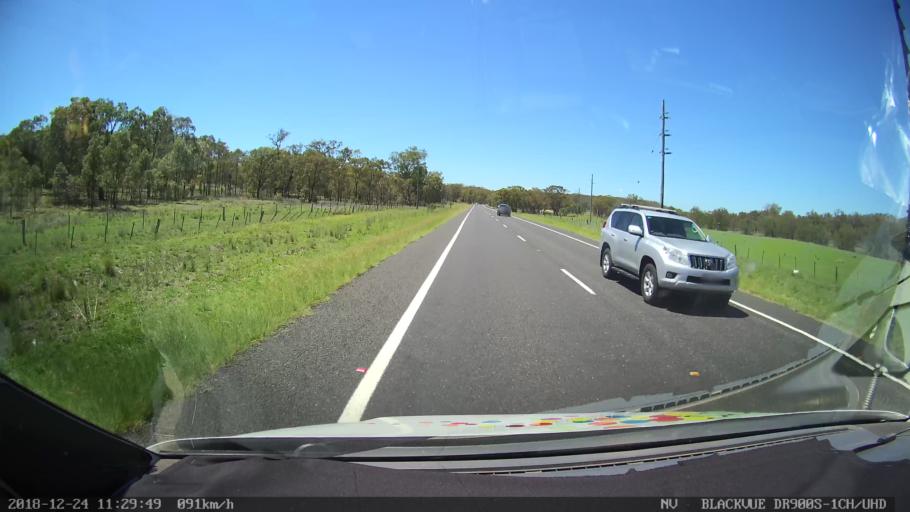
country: AU
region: New South Wales
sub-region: Upper Hunter Shire
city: Merriwa
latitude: -32.1970
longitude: 150.4652
